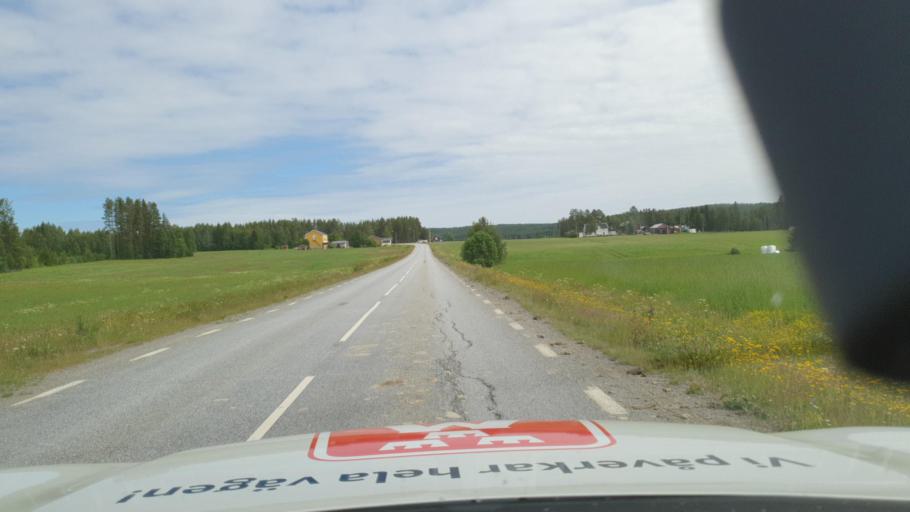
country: SE
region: Vaesterbotten
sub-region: Skelleftea Kommun
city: Burtraesk
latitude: 64.6085
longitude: 20.5872
